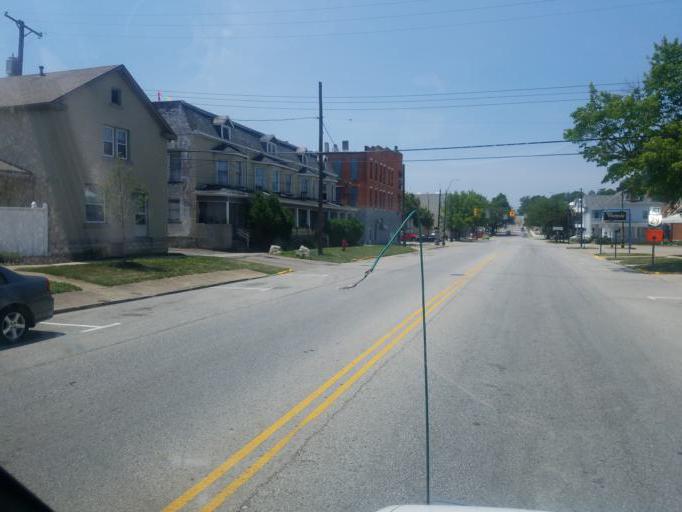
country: US
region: Ohio
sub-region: Shelby County
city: Sidney
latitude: 40.2869
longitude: -84.1540
